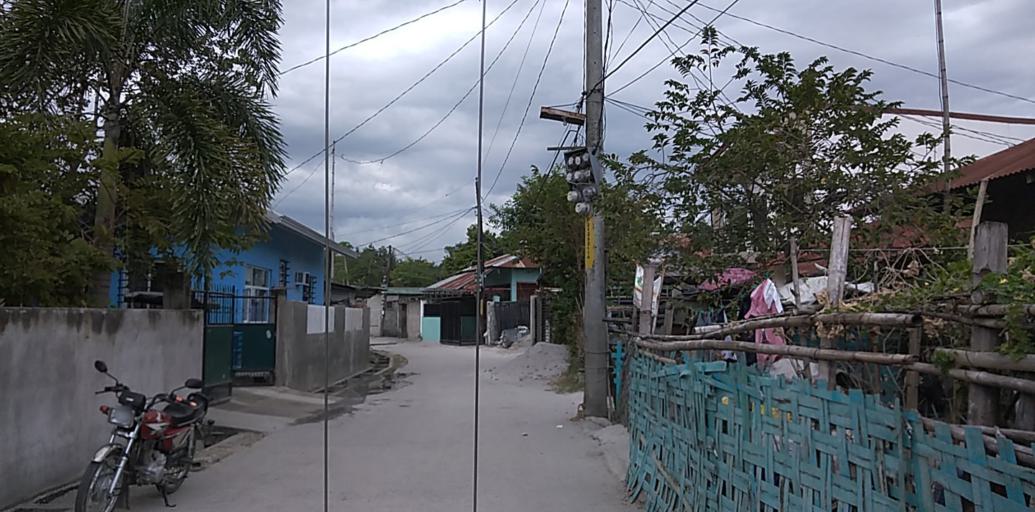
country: PH
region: Central Luzon
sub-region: Province of Pampanga
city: Pulung Santol
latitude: 15.0403
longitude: 120.5664
